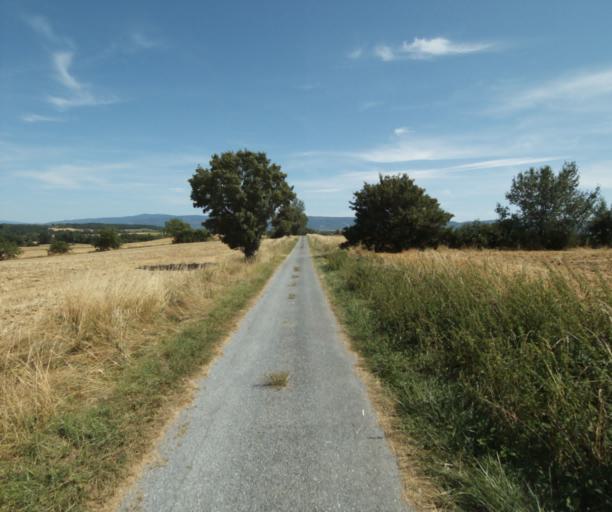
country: FR
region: Midi-Pyrenees
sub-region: Departement du Tarn
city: Puylaurens
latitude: 43.5397
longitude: 2.0156
